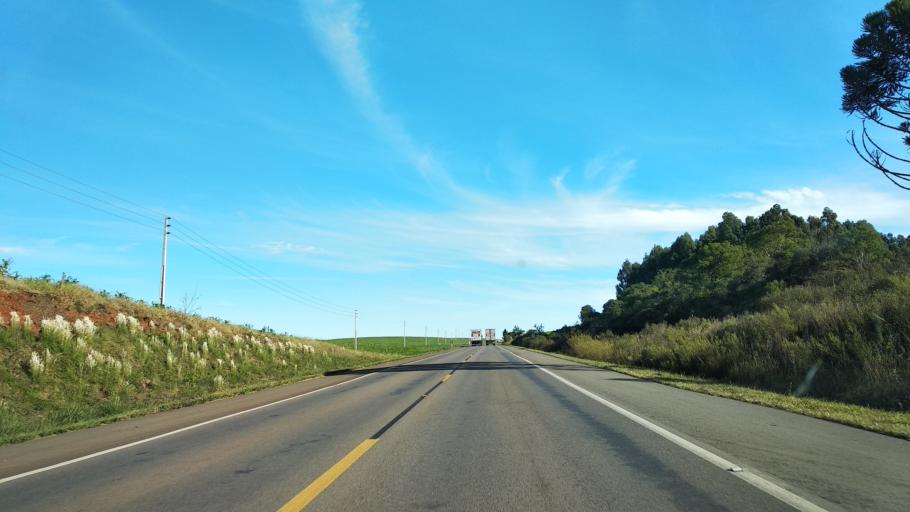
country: BR
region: Santa Catarina
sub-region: Celso Ramos
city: Celso Ramos
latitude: -27.5146
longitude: -51.3490
